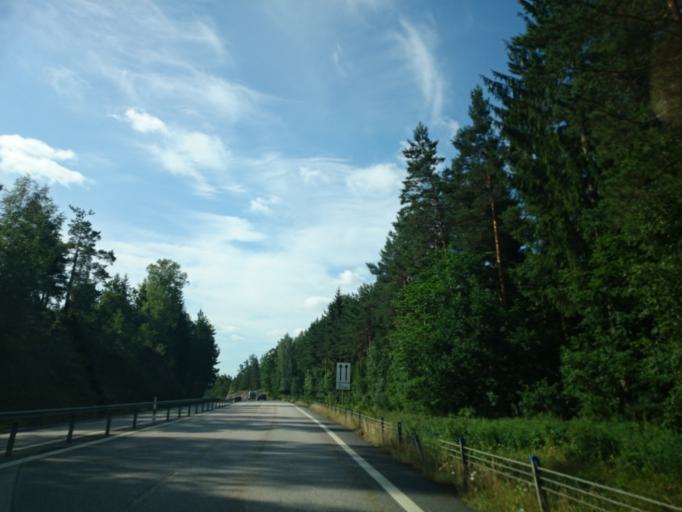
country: SE
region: Kalmar
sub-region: Vasterviks Kommun
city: Forserum
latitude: 58.0306
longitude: 16.5150
